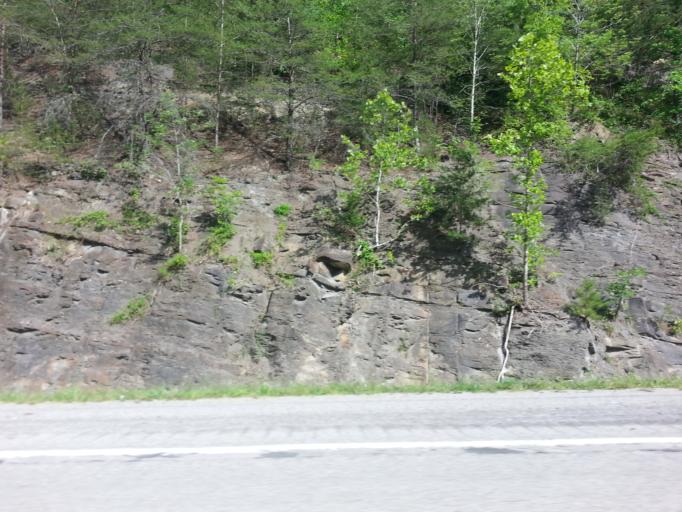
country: US
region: Kentucky
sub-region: Harlan County
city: Harlan
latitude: 36.8753
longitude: -83.2987
